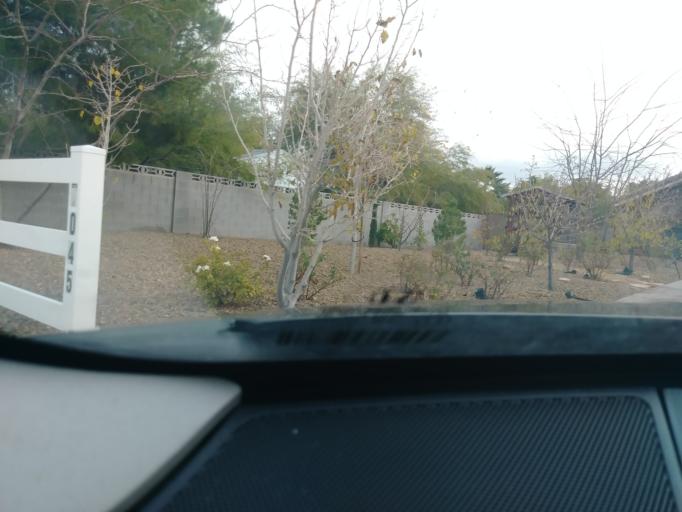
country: US
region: Nevada
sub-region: Clark County
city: Spring Valley
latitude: 36.1403
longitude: -115.2461
